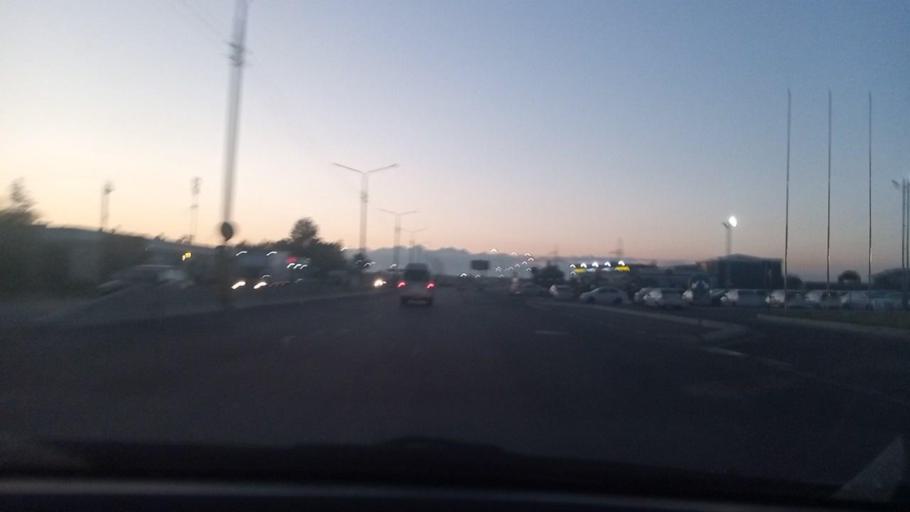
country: UZ
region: Toshkent Shahri
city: Tashkent
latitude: 41.2440
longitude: 69.2322
